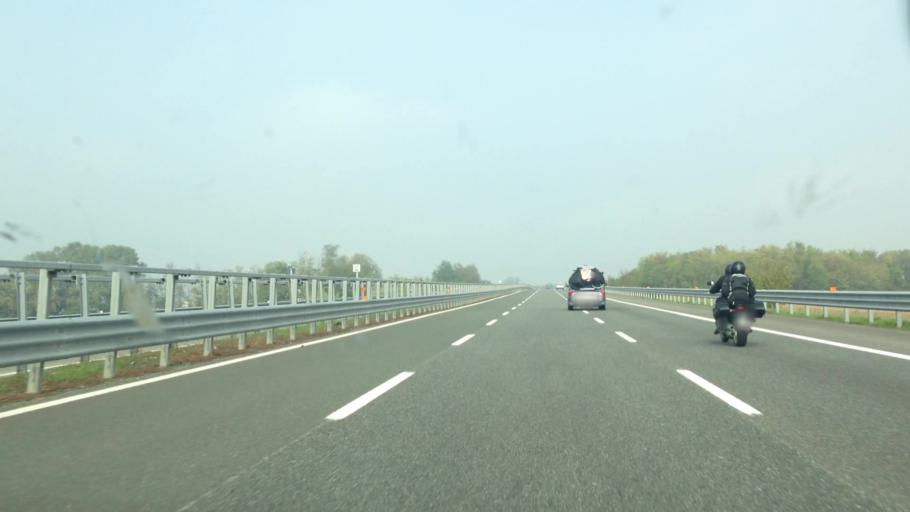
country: IT
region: Piedmont
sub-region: Provincia di Alessandria
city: Mirabello Monferrato
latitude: 45.0497
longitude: 8.5215
